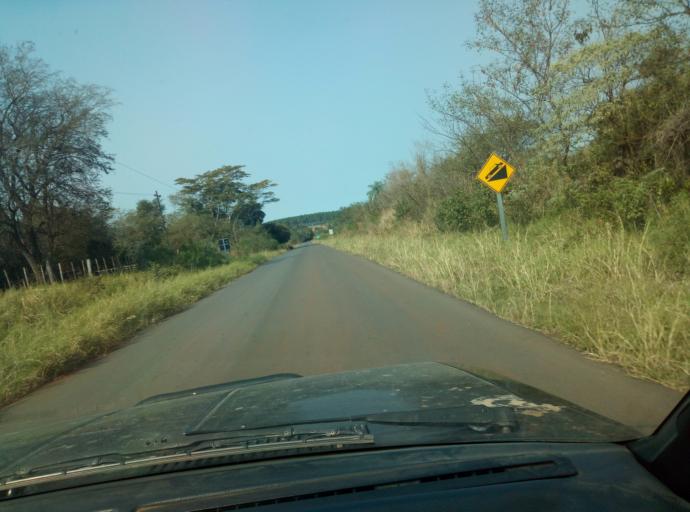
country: PY
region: Caaguazu
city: Carayao
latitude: -25.2367
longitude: -56.2868
